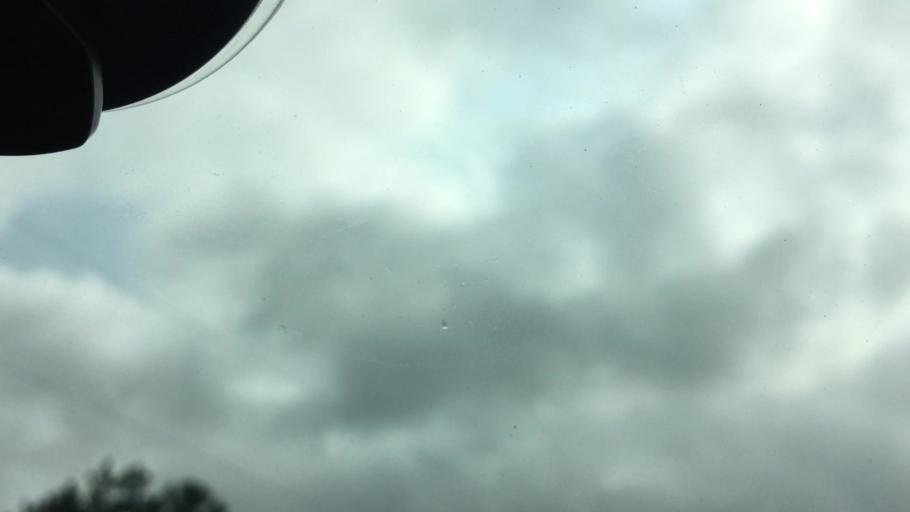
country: US
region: Georgia
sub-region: Henry County
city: McDonough
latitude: 33.4327
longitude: -84.1690
